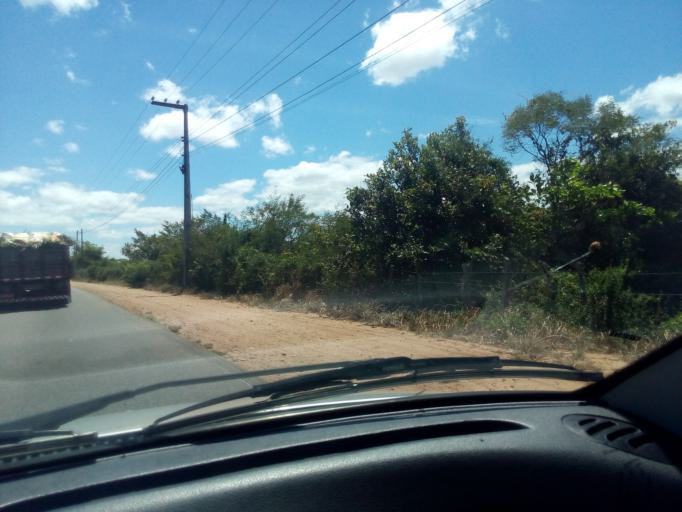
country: BR
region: Rio Grande do Norte
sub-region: Sao Goncalo Do Amarante
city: Sao Goncalo do Amarante
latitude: -5.7976
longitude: -35.3293
